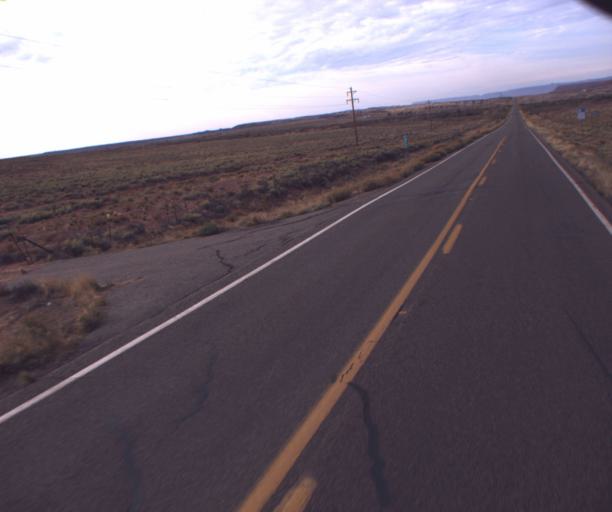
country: US
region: Arizona
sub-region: Apache County
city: Many Farms
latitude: 36.5004
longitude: -109.4837
